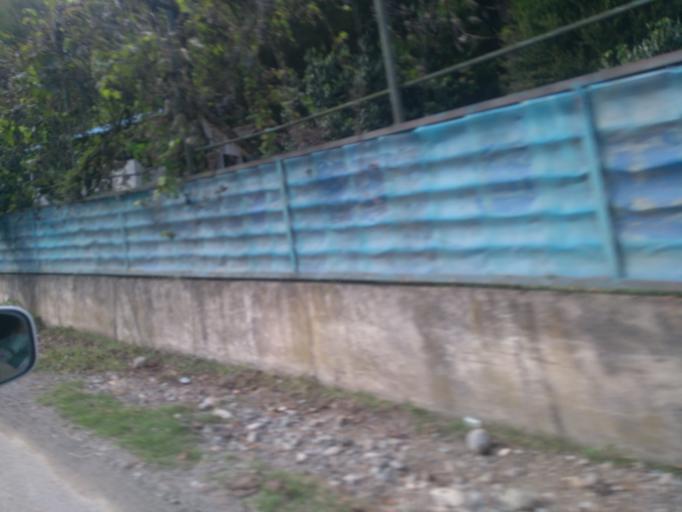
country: TR
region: Artvin
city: Muratli
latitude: 41.5438
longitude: 41.7230
